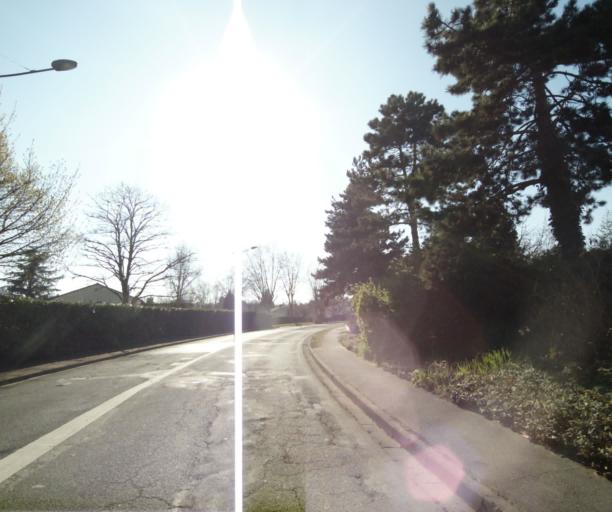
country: FR
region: Ile-de-France
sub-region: Departement du Val-d'Oise
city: Cergy
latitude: 49.0288
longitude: 2.0870
